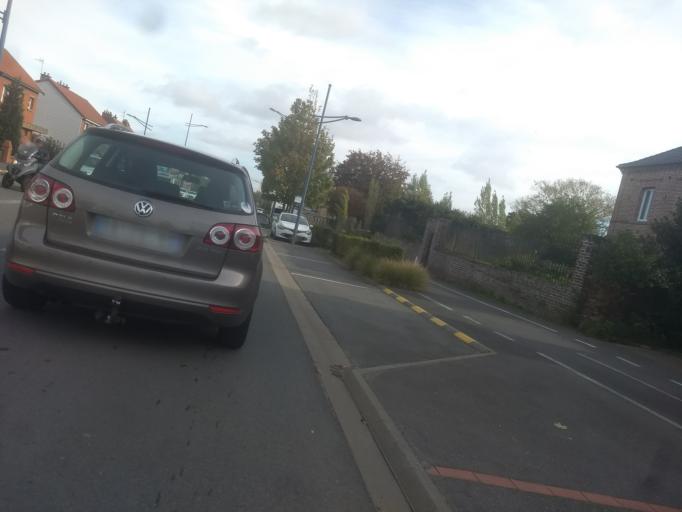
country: FR
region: Nord-Pas-de-Calais
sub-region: Departement du Pas-de-Calais
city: Dainville
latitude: 50.2803
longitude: 2.7321
